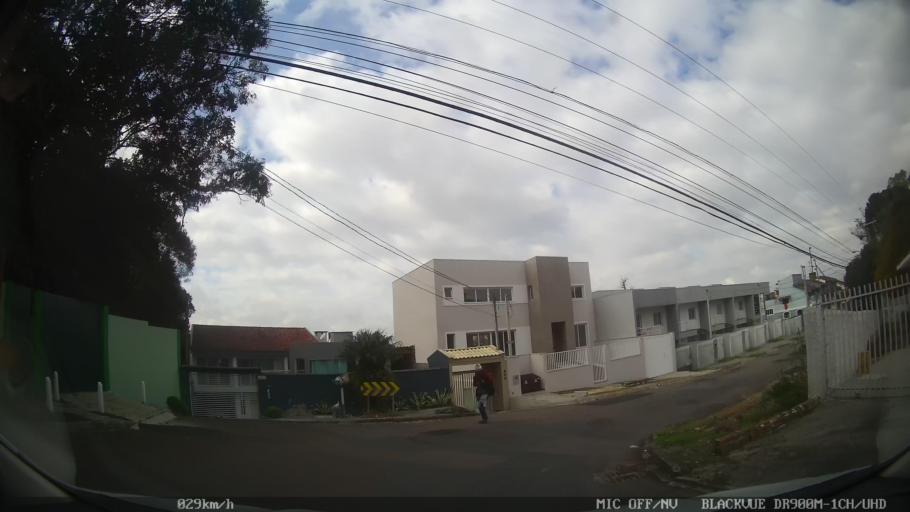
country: BR
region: Parana
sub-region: Curitiba
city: Curitiba
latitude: -25.3698
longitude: -49.2557
